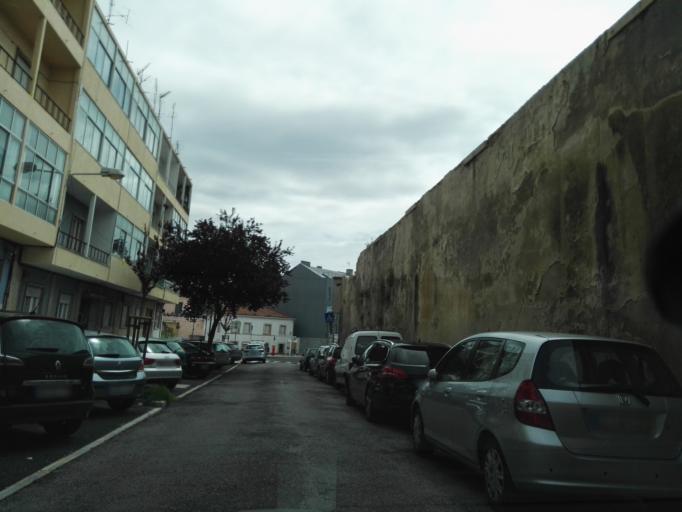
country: PT
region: Setubal
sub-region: Almada
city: Pragal
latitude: 38.7020
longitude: -9.1918
